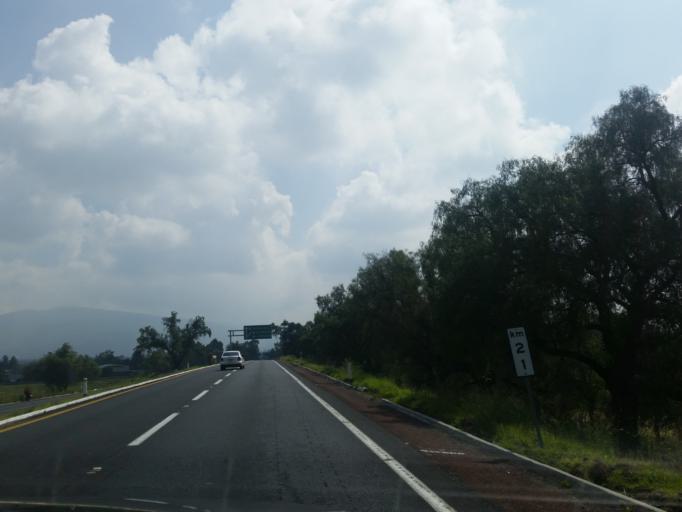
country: MX
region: Morelos
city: Teotihuacan de Arista
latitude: 19.6739
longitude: -98.8645
